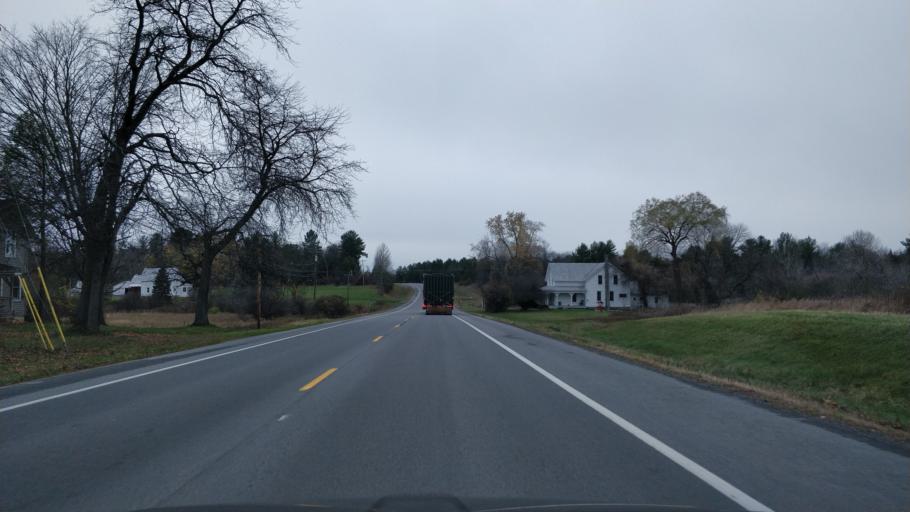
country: CA
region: Ontario
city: Brockville
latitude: 44.6120
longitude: -75.6040
